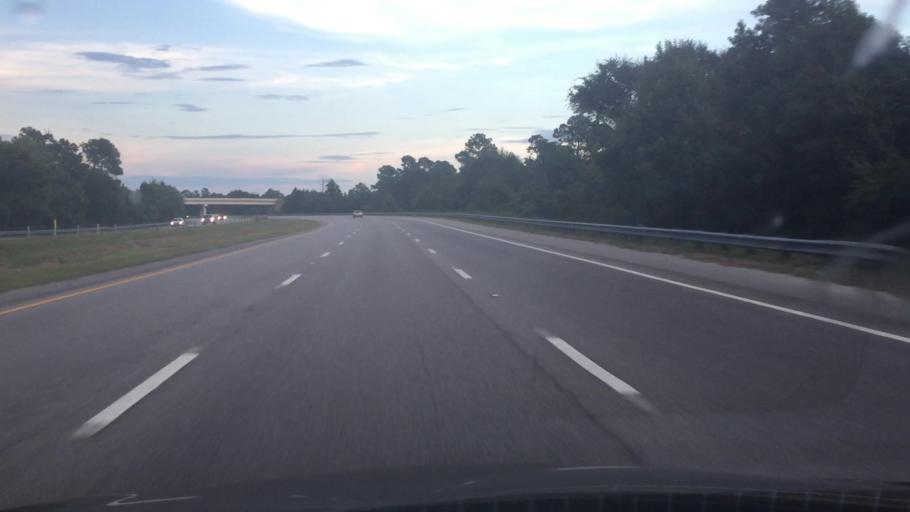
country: US
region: South Carolina
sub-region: Horry County
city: North Myrtle Beach
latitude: 33.8256
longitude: -78.7288
